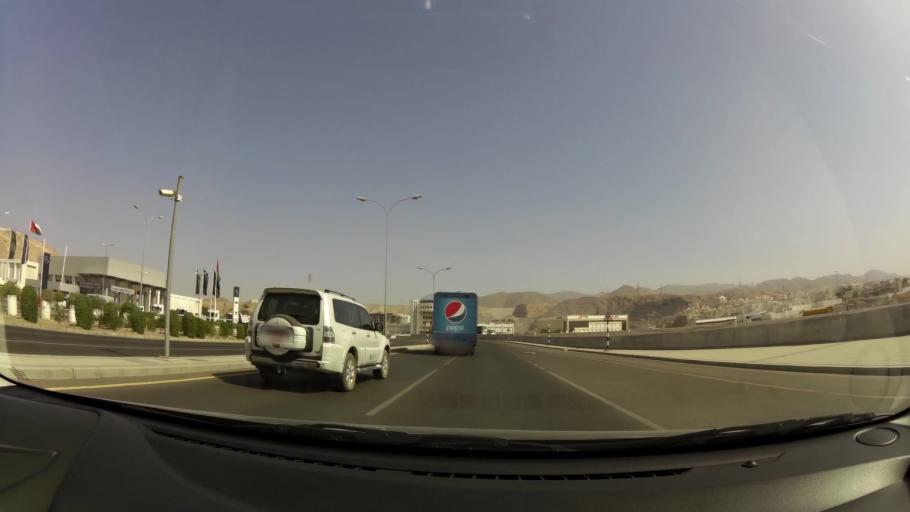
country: OM
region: Muhafazat Masqat
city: Muscat
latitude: 23.6103
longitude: 58.4993
